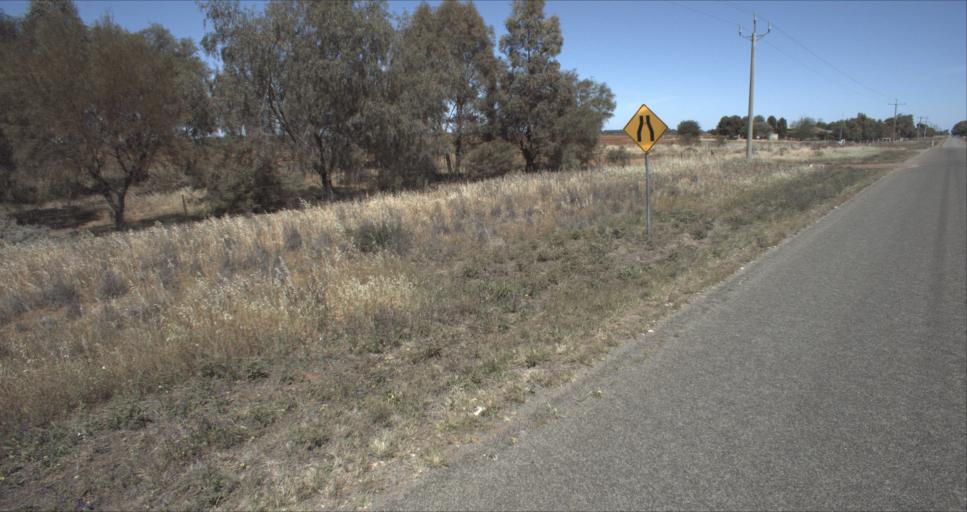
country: AU
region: New South Wales
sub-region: Leeton
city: Leeton
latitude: -34.5811
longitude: 146.2897
